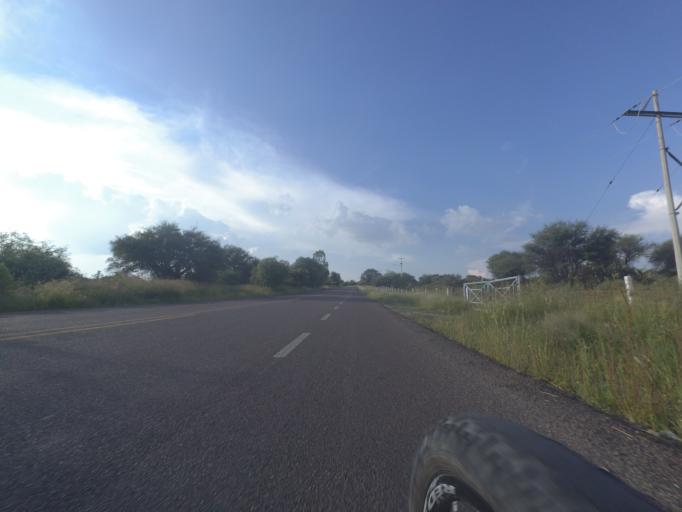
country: MX
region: Aguascalientes
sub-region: Aguascalientes
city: Penuelas (El Cienegal)
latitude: 21.7611
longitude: -102.3510
